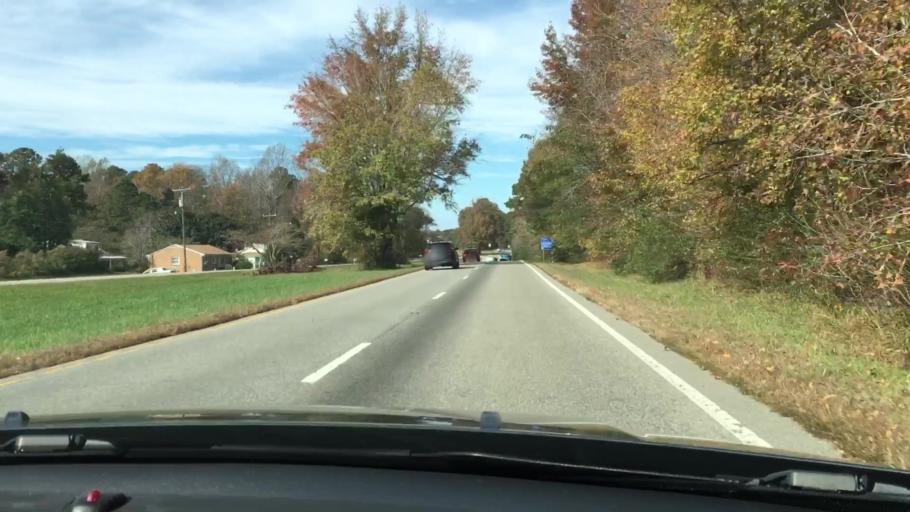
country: US
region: Virginia
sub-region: James City County
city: Williamsburg
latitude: 37.3293
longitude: -76.7421
